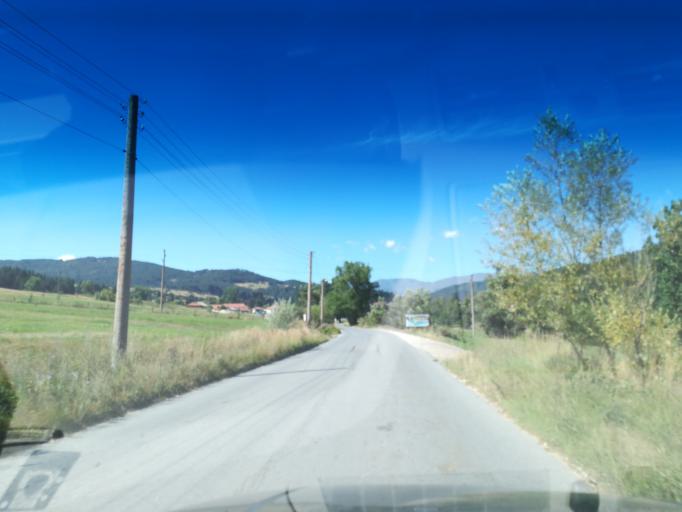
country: BG
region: Sofiya
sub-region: Obshtina Koprivshtitsa
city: Koprivshtitsa
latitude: 42.6250
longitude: 24.3665
